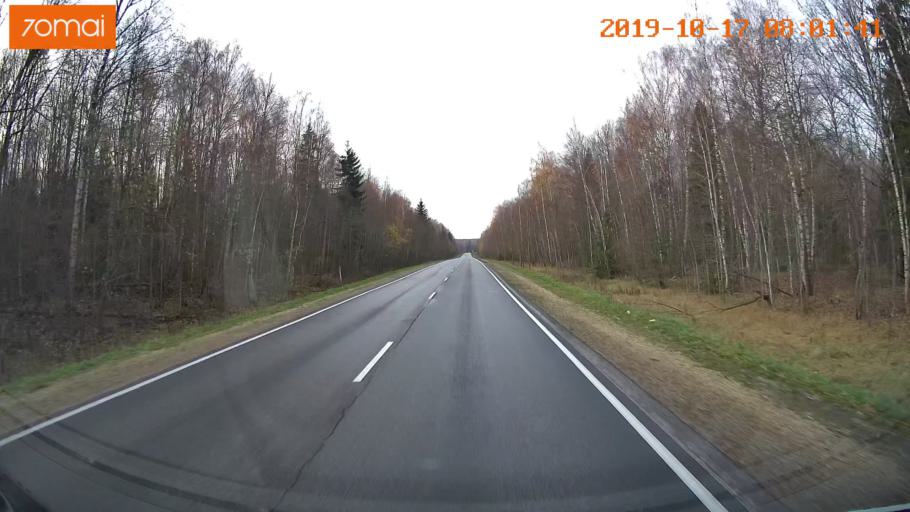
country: RU
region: Vladimir
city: Bavleny
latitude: 56.3704
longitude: 39.4913
